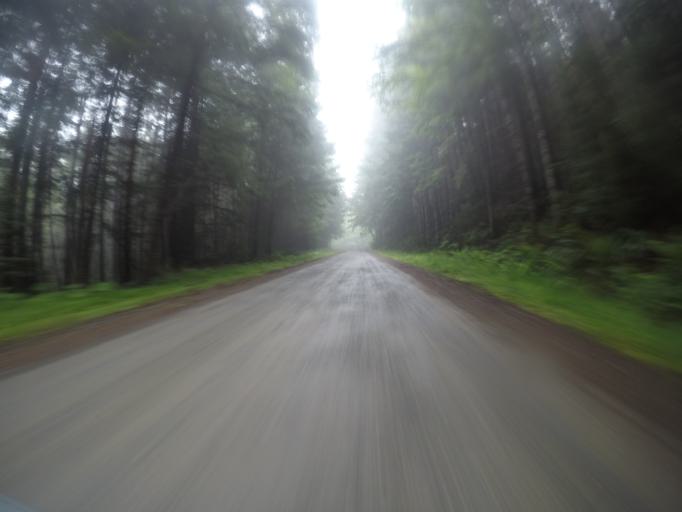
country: US
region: California
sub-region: Humboldt County
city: Westhaven-Moonstone
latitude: 41.2293
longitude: -123.9925
